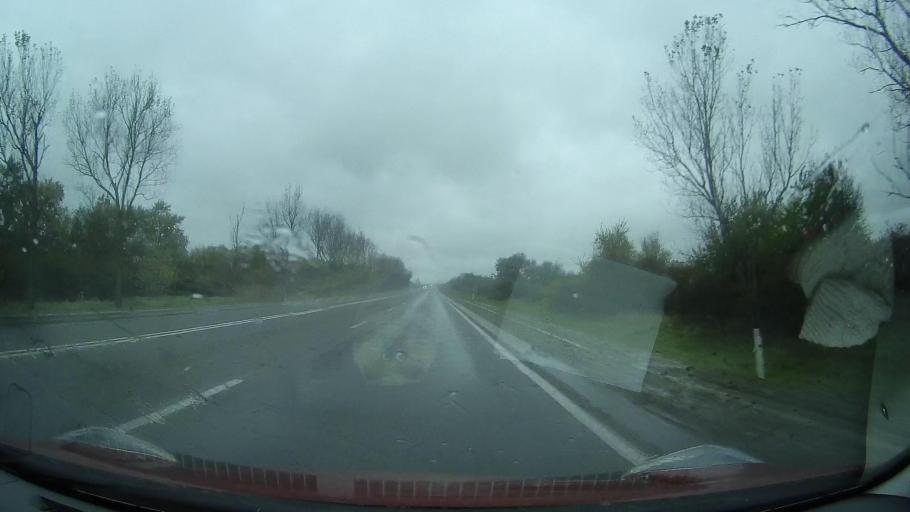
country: RU
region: Stavropol'skiy
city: Nevinnomyssk
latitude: 44.6302
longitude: 42.0309
